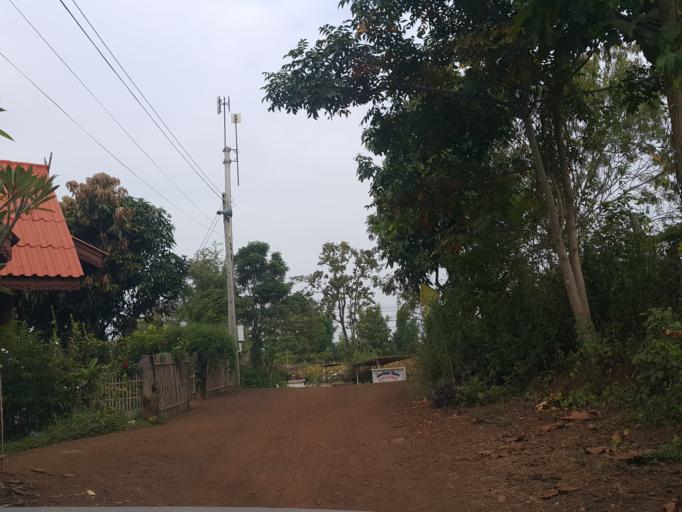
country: TH
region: Chiang Mai
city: Pai
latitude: 19.3641
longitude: 98.4500
